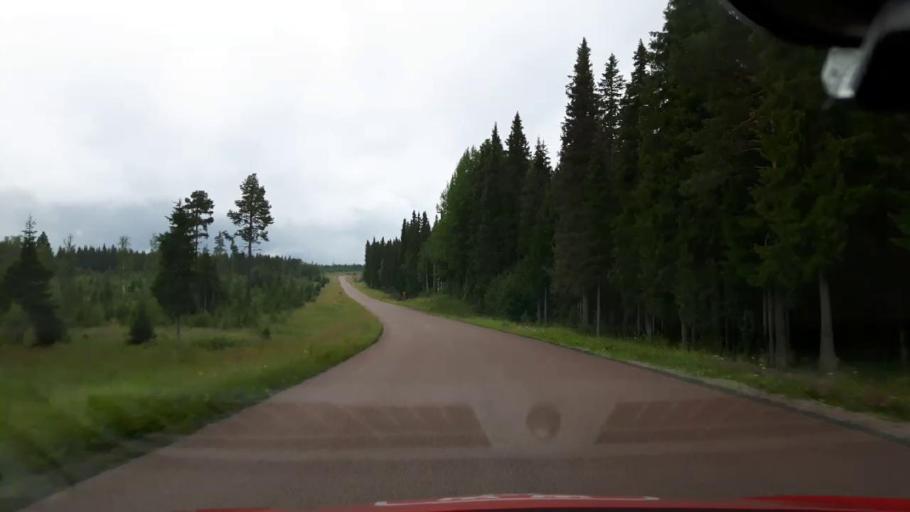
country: SE
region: Jaemtland
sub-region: Krokoms Kommun
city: Valla
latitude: 63.3804
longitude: 13.7590
